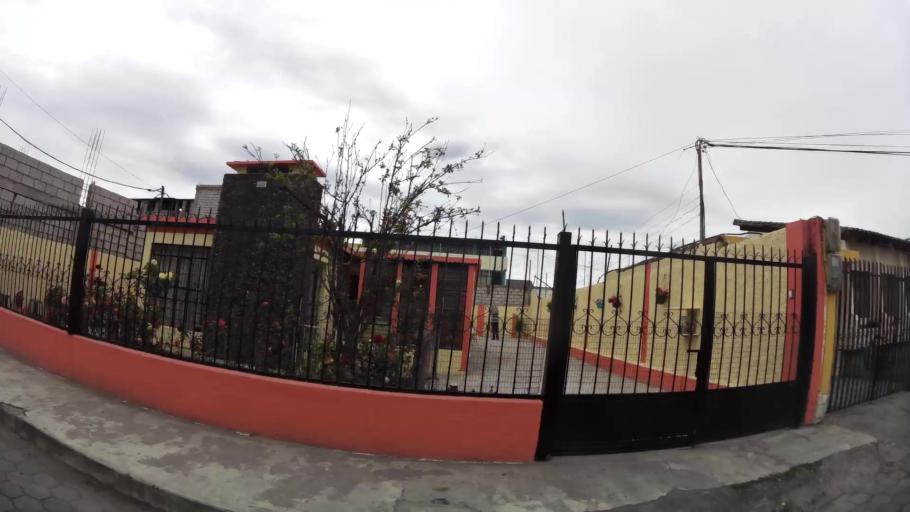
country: EC
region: Cotopaxi
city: Latacunga
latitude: -0.9408
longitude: -78.6129
